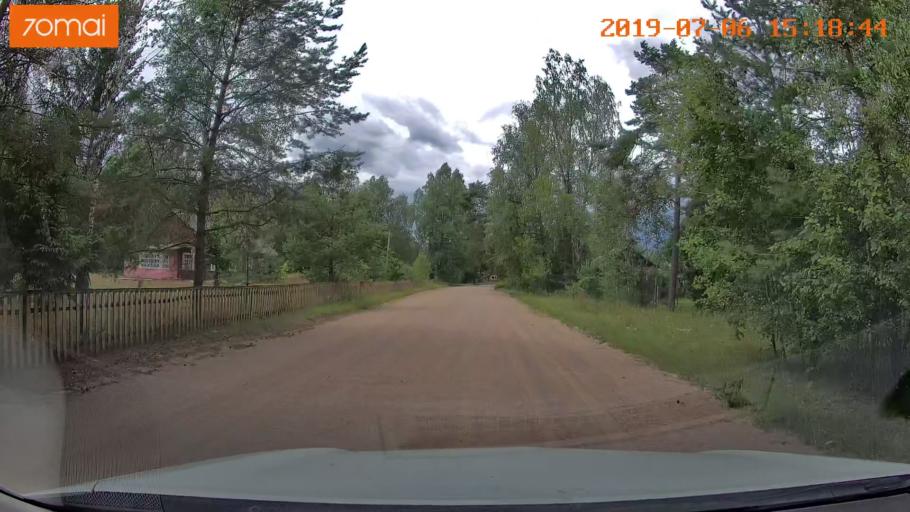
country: BY
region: Minsk
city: Ivyanyets
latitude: 53.9933
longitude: 26.6509
